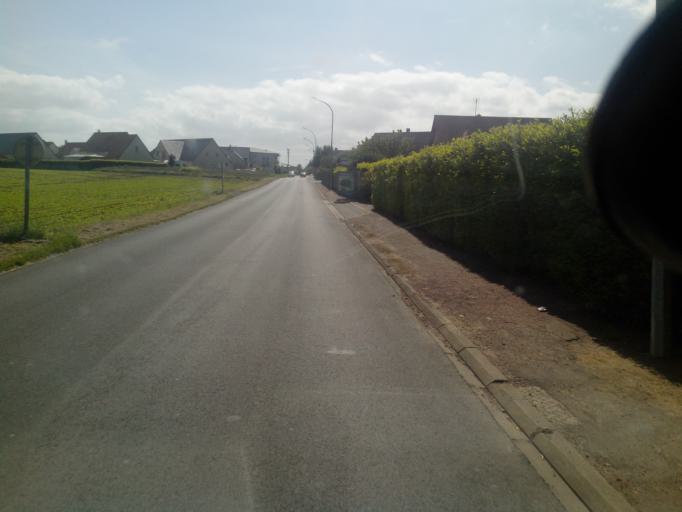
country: FR
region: Lower Normandy
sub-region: Departement du Calvados
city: Courseulles-sur-Mer
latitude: 49.3248
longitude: -0.4486
